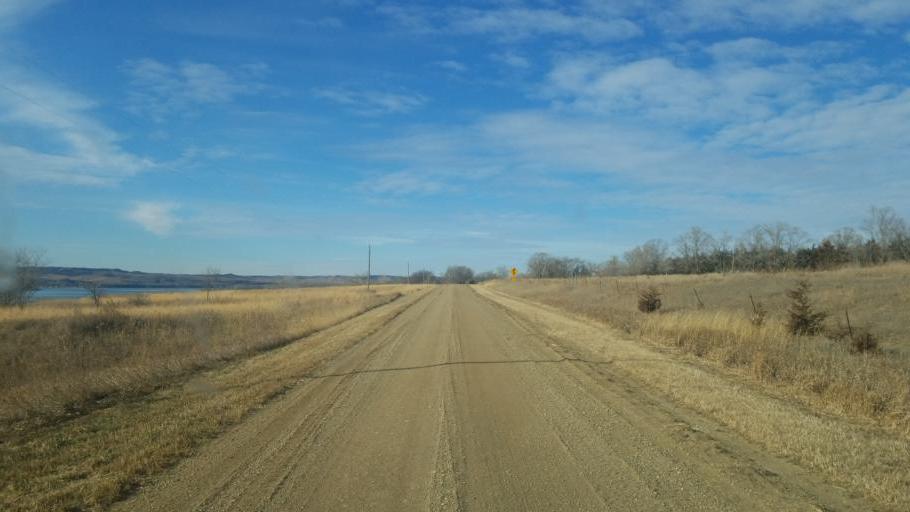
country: US
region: South Dakota
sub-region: Charles Mix County
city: Wagner
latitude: 42.9288
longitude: -98.4042
